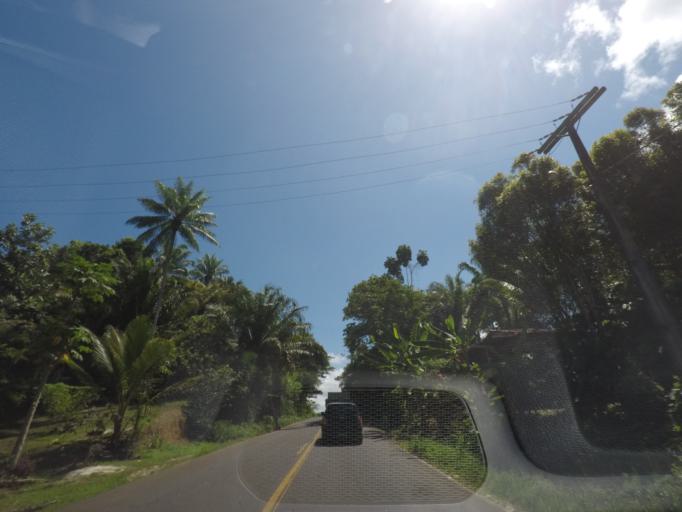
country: BR
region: Bahia
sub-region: Valenca
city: Valenca
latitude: -13.4515
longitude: -39.0864
